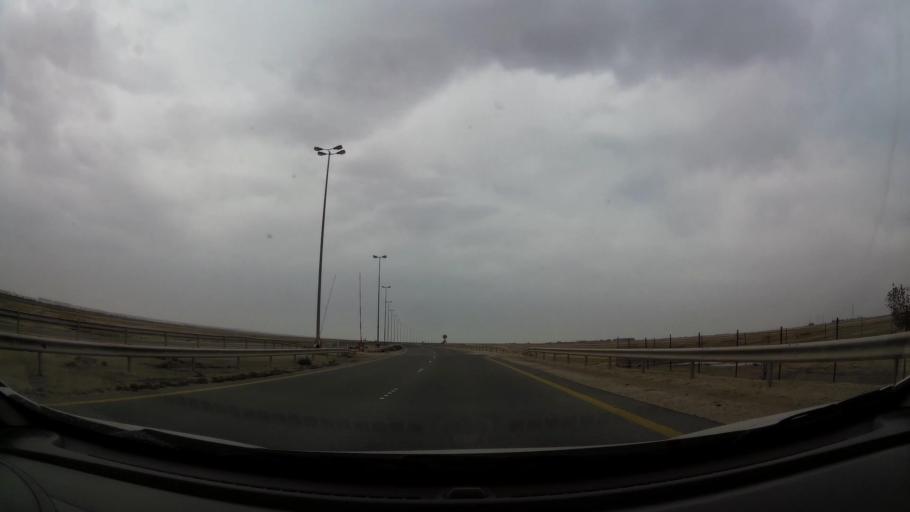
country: BH
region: Central Governorate
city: Dar Kulayb
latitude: 26.0110
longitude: 50.4835
